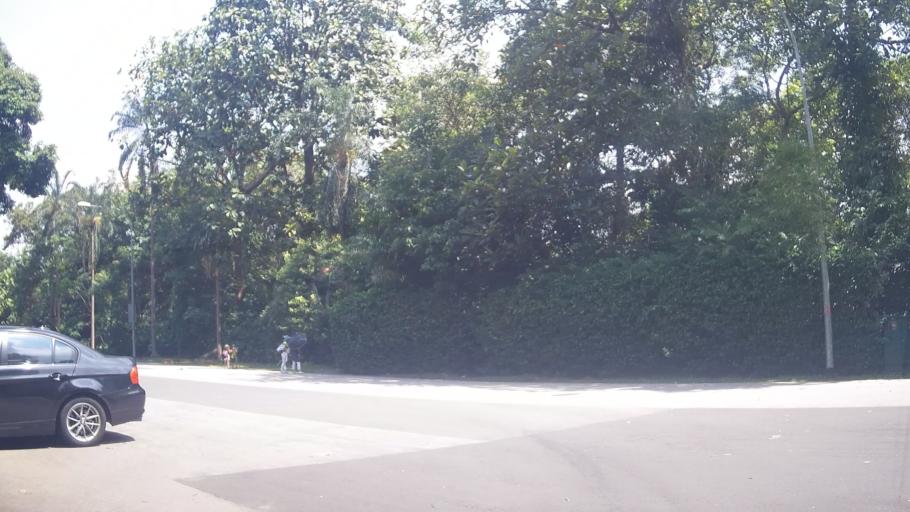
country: SG
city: Singapore
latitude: 1.3507
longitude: 103.7668
